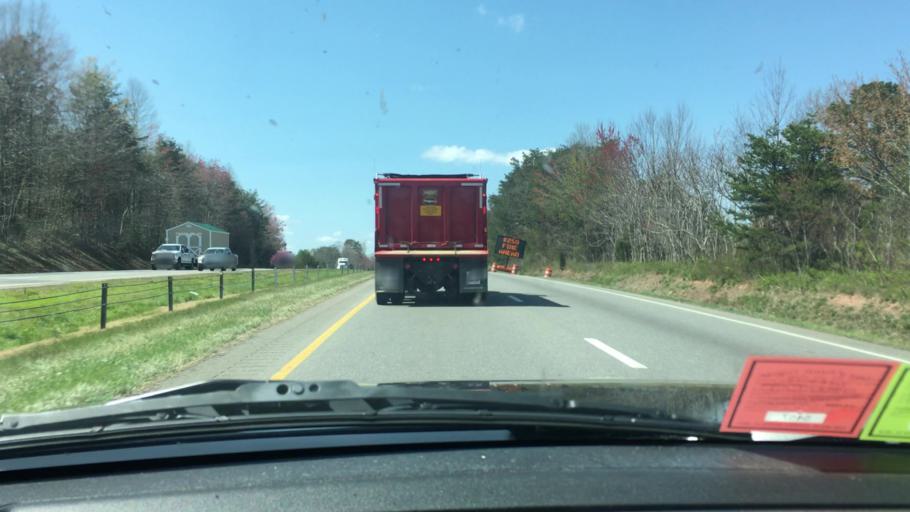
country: US
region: North Carolina
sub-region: Surry County
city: Pilot Mountain
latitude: 36.4276
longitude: -80.5224
